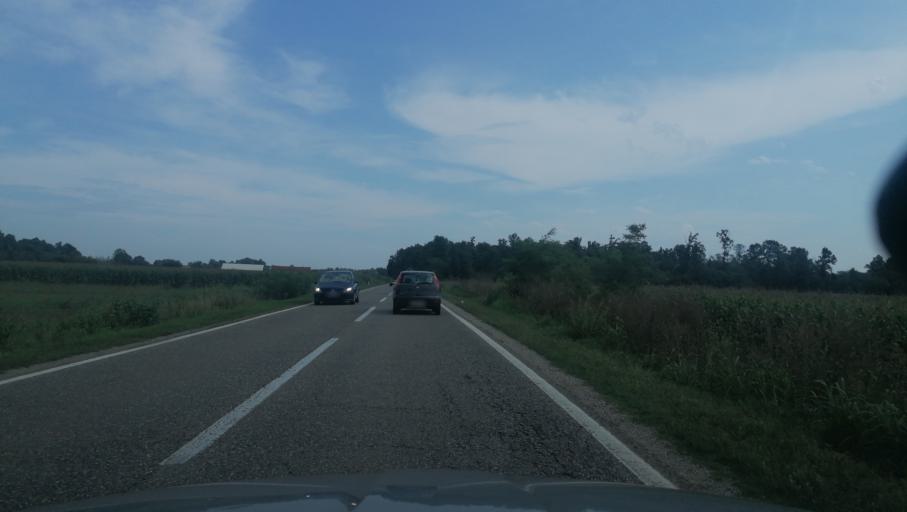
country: HR
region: Vukovarsko-Srijemska
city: Soljani
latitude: 44.8309
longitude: 19.0009
